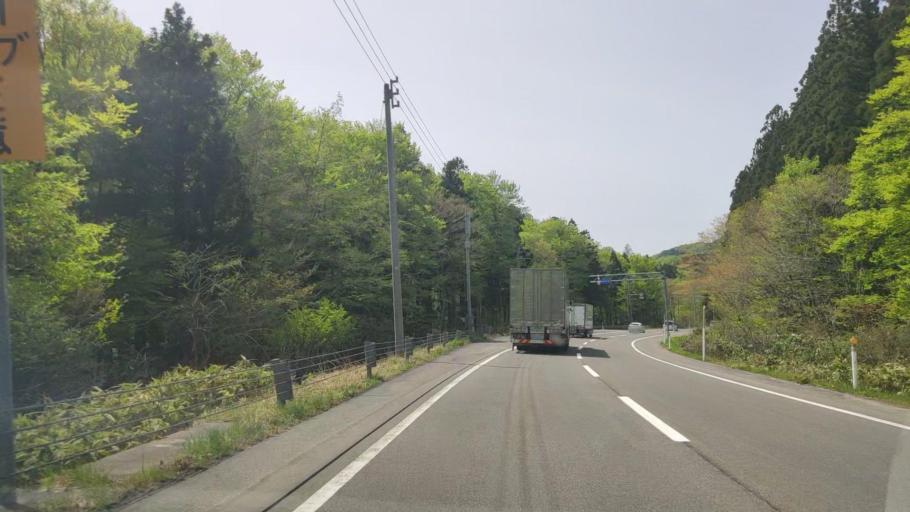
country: JP
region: Aomori
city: Aomori Shi
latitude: 40.7757
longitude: 141.0119
